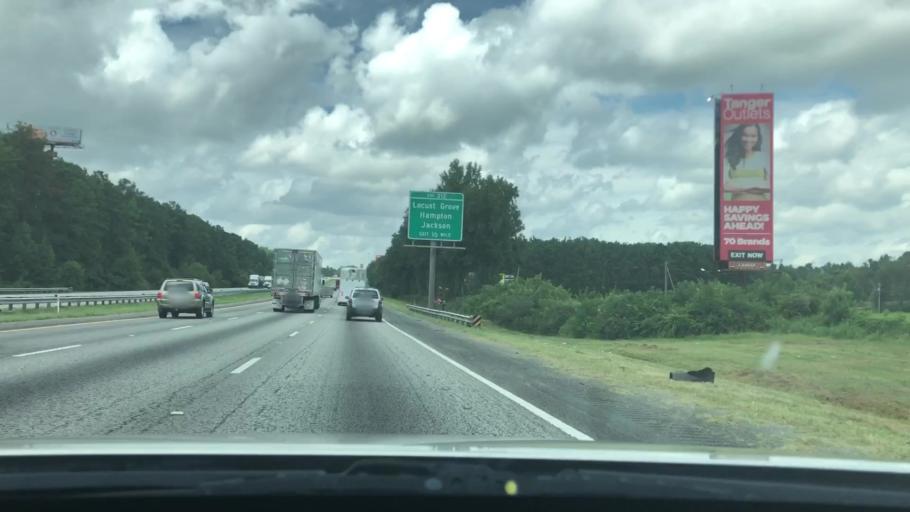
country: US
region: Georgia
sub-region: Henry County
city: Locust Grove
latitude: 33.3415
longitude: -84.1232
